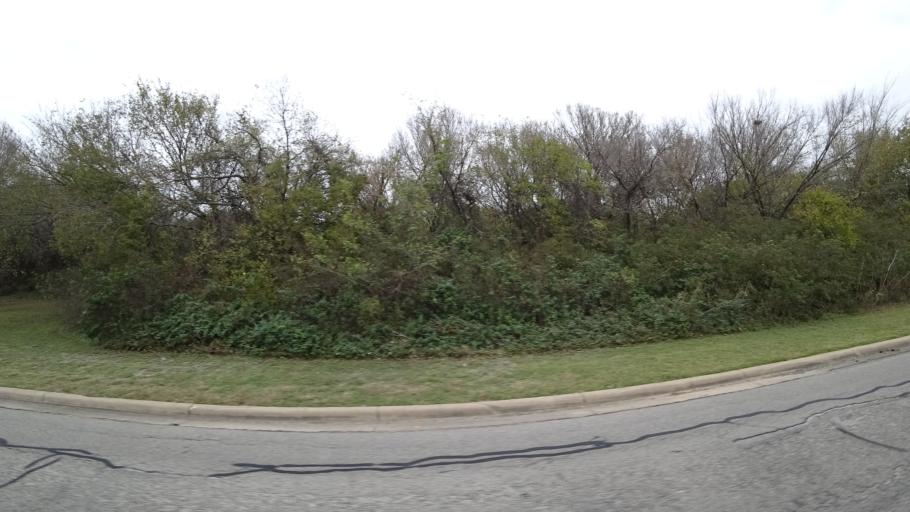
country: US
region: Texas
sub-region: Travis County
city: Pflugerville
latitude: 30.4485
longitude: -97.6177
